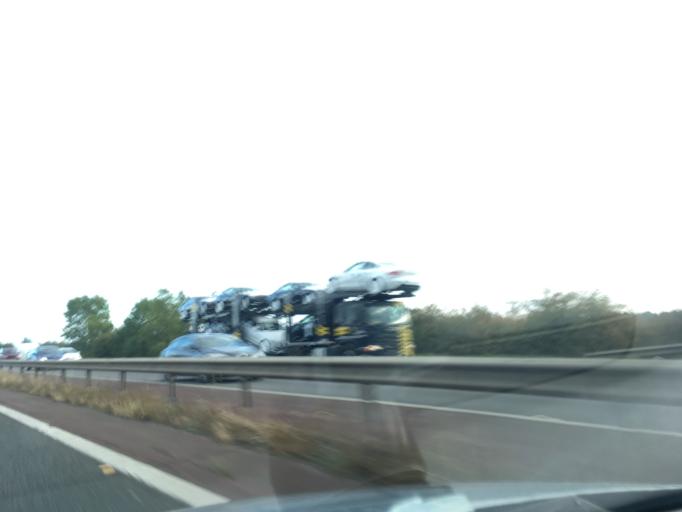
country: GB
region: England
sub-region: Oxfordshire
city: Adderbury
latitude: 52.0471
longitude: -1.3056
